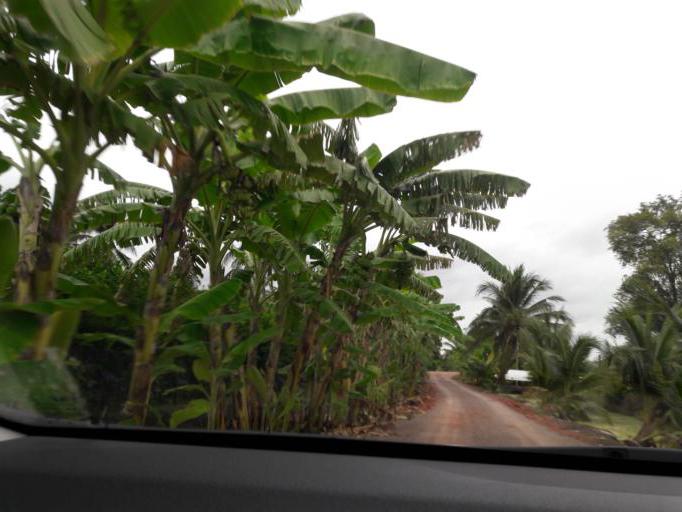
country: TH
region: Samut Sakhon
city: Ban Phaeo
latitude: 13.5470
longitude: 100.0360
